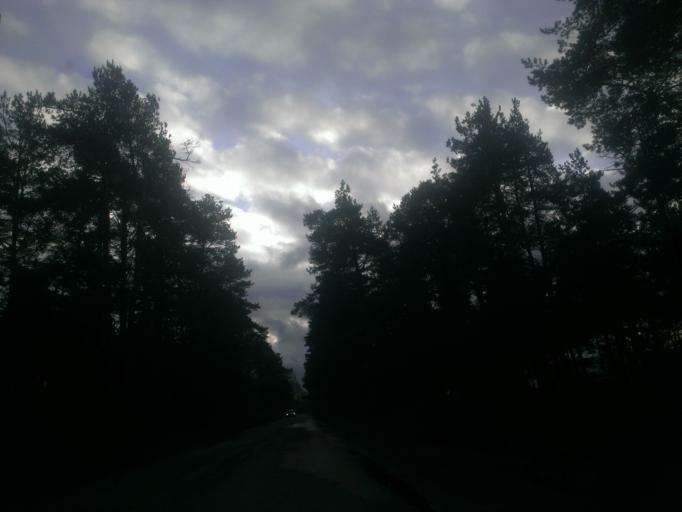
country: LV
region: Riga
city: Bolderaja
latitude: 57.0558
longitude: 24.0726
